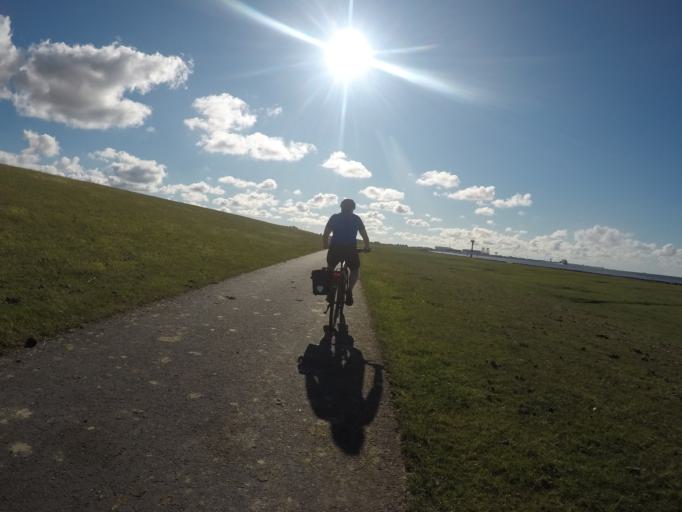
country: DE
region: Lower Saxony
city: Nordleda
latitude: 53.8319
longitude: 8.8020
